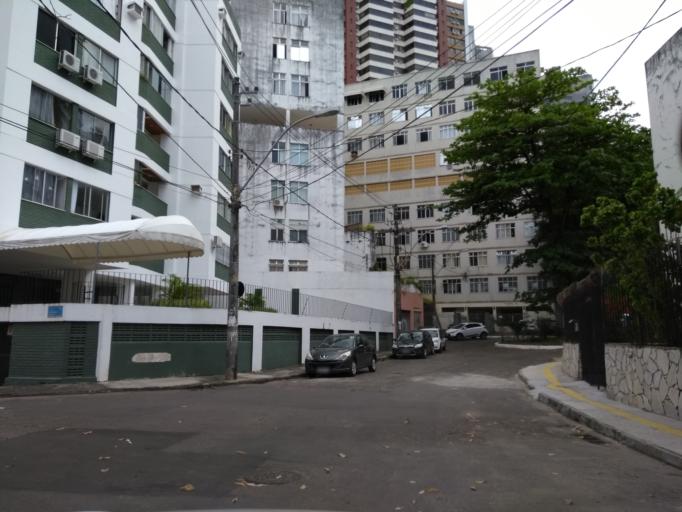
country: BR
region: Bahia
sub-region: Salvador
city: Salvador
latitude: -13.0005
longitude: -38.5279
